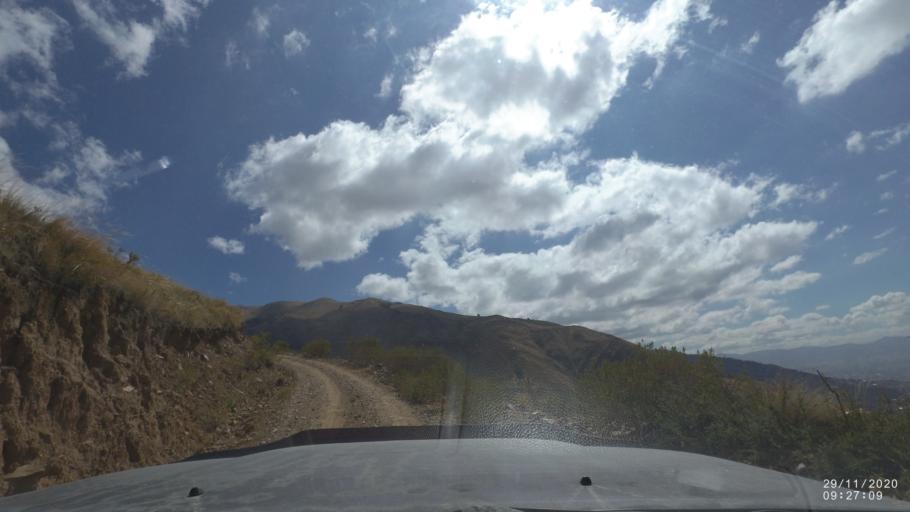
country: BO
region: Cochabamba
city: Cochabamba
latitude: -17.3185
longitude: -66.1869
